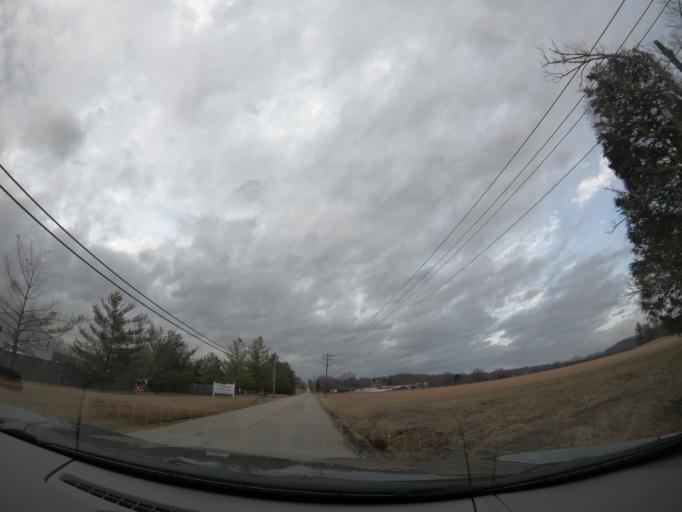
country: US
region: Indiana
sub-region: Floyd County
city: Galena
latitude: 38.3586
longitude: -85.9198
